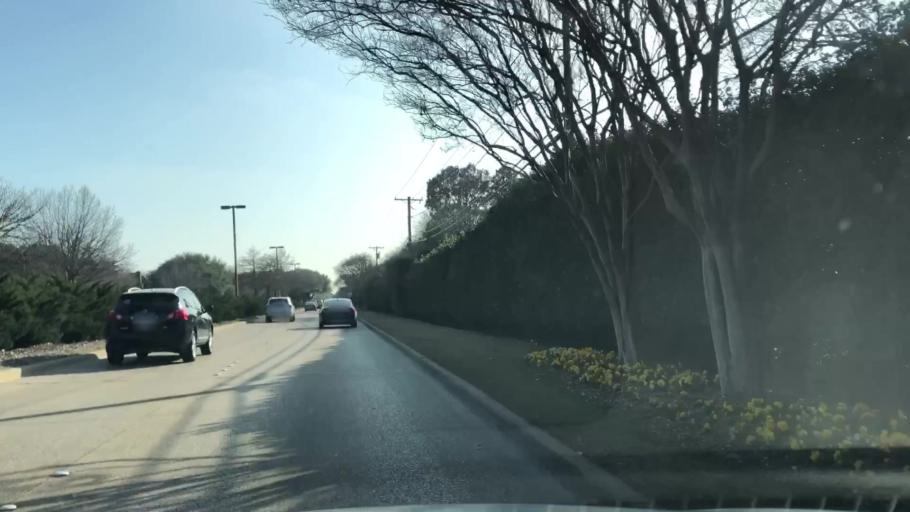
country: US
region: Texas
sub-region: Dallas County
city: Addison
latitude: 32.9457
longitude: -96.8558
